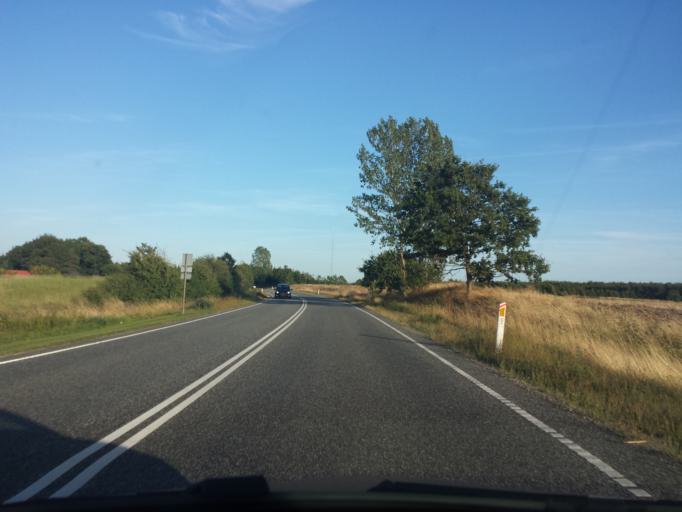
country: DK
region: Zealand
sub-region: Roskilde Kommune
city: Jyllinge
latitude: 55.7838
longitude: 12.1222
